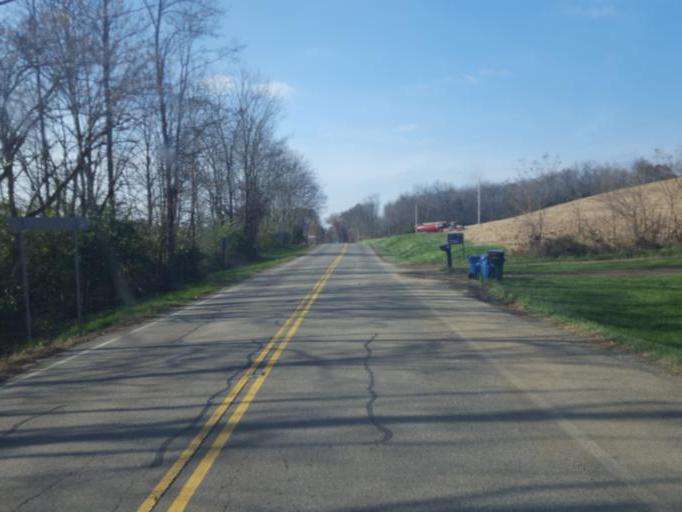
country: US
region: Ohio
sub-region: Knox County
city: Oak Hill
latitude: 40.3894
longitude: -82.2605
